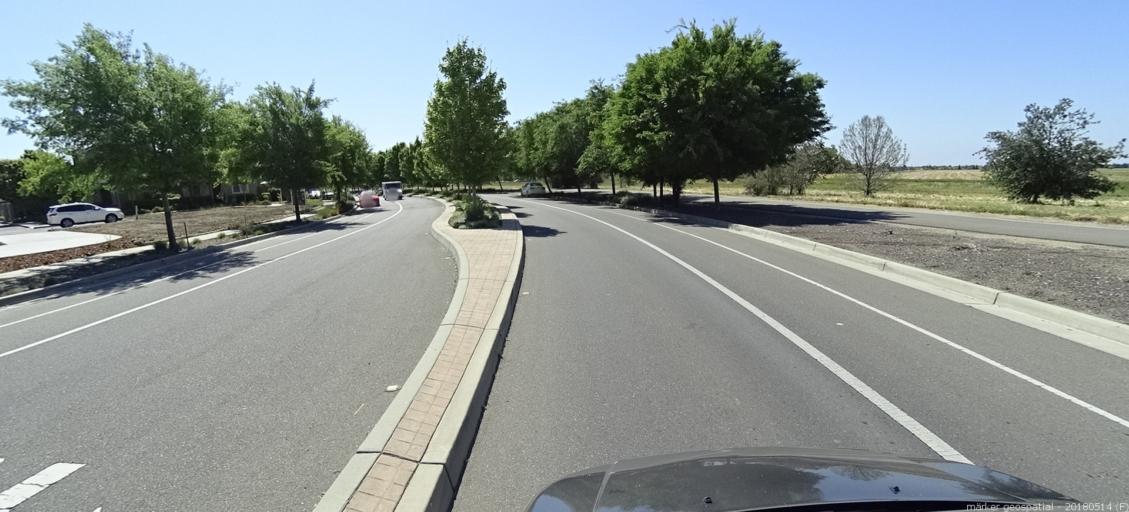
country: US
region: California
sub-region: Yolo County
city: West Sacramento
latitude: 38.6442
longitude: -121.5438
